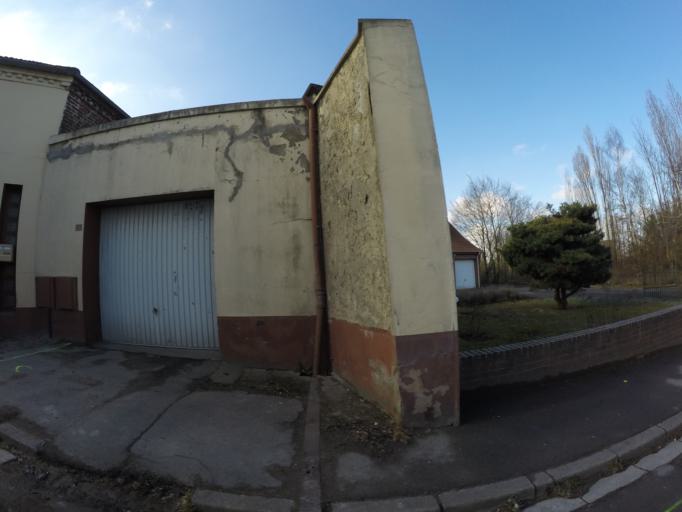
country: FR
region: Nord-Pas-de-Calais
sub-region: Departement du Pas-de-Calais
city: Bully-les-Mines
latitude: 50.4552
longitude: 2.7283
